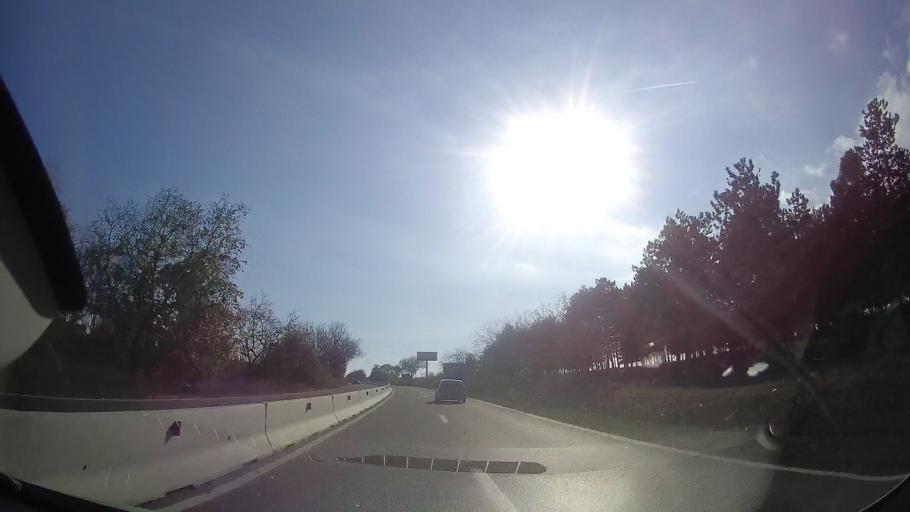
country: RO
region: Constanta
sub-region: Comuna Douazeci si Trei August
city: Douazeci si Trei August
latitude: 43.9002
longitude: 28.5709
